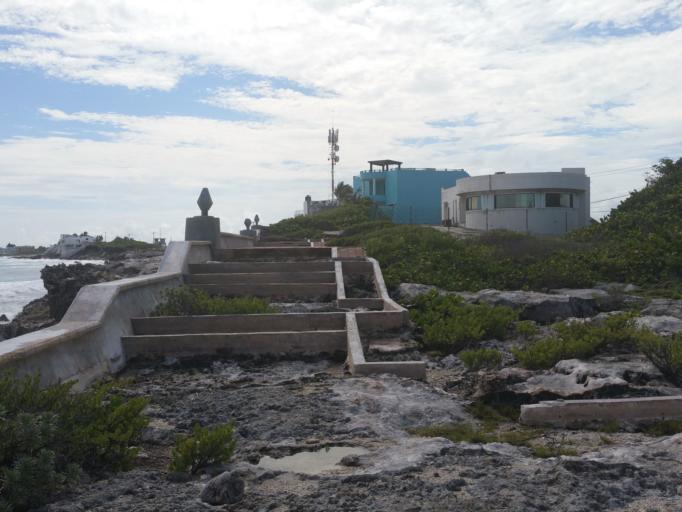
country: MX
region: Quintana Roo
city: Isla Mujeres
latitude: 21.2514
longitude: -86.7422
